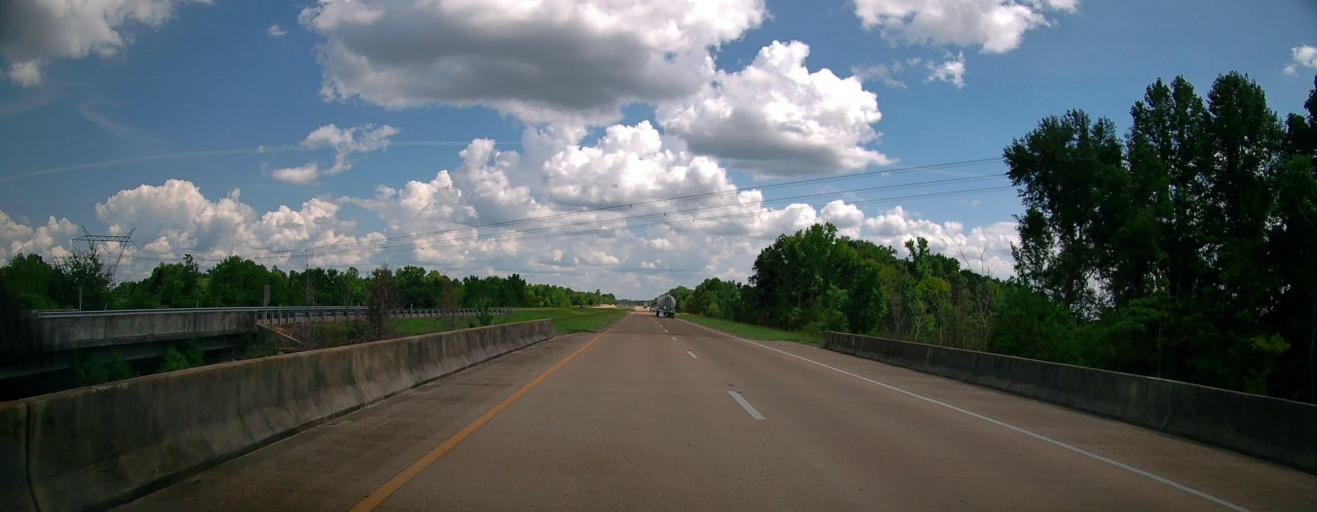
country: US
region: Mississippi
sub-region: Lowndes County
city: Columbus Air Force Base
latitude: 33.6796
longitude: -88.4326
